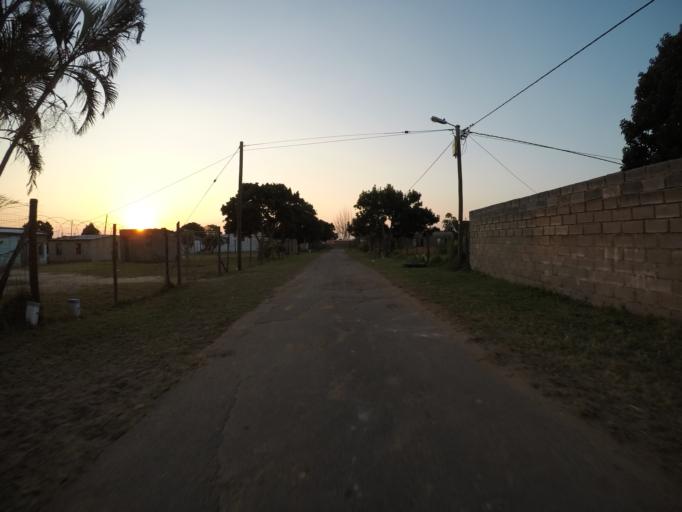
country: ZA
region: KwaZulu-Natal
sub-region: uThungulu District Municipality
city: Richards Bay
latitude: -28.7604
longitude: 32.1269
